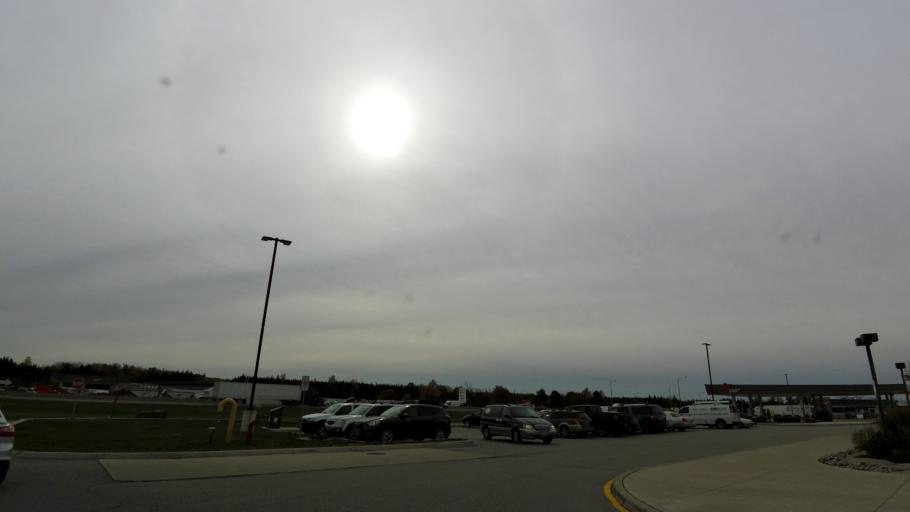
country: CA
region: Ontario
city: Cambridge
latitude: 43.4351
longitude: -80.2458
